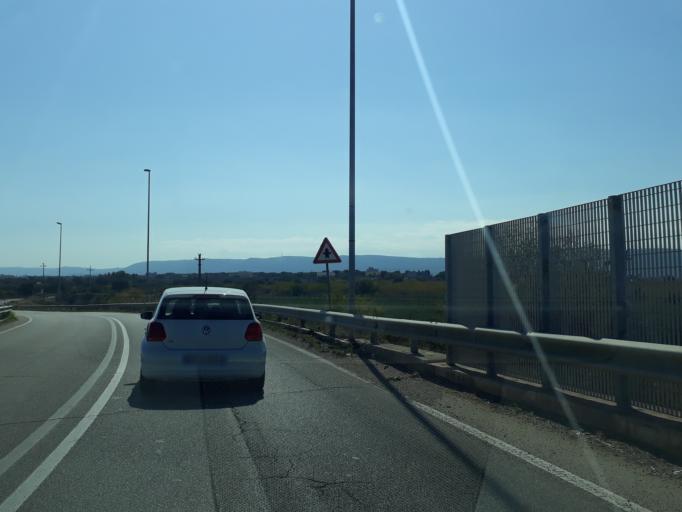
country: IT
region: Apulia
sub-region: Provincia di Bari
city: Monopoli
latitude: 40.9210
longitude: 17.3152
